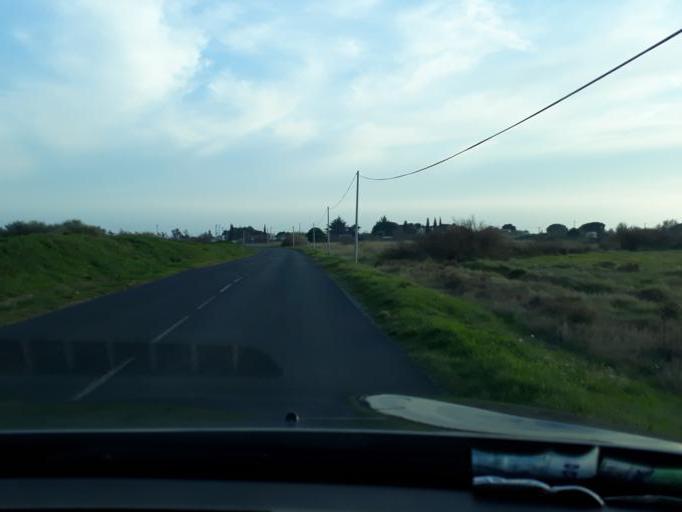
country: FR
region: Languedoc-Roussillon
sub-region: Departement de l'Herault
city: Marseillan
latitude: 43.3339
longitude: 3.5316
